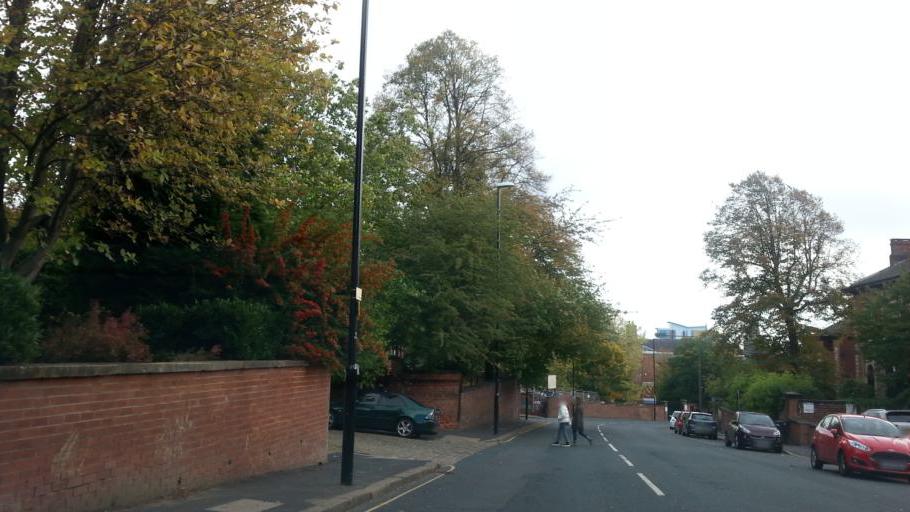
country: GB
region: England
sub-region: City and Borough of Leeds
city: Leeds
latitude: 53.8032
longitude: -1.5590
